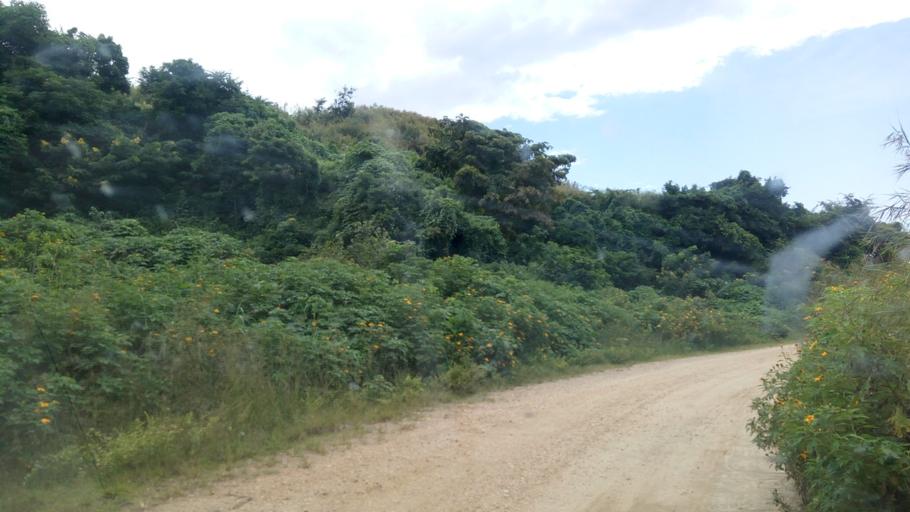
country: CD
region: South Kivu
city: Uvira
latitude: -3.5221
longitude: 29.1489
